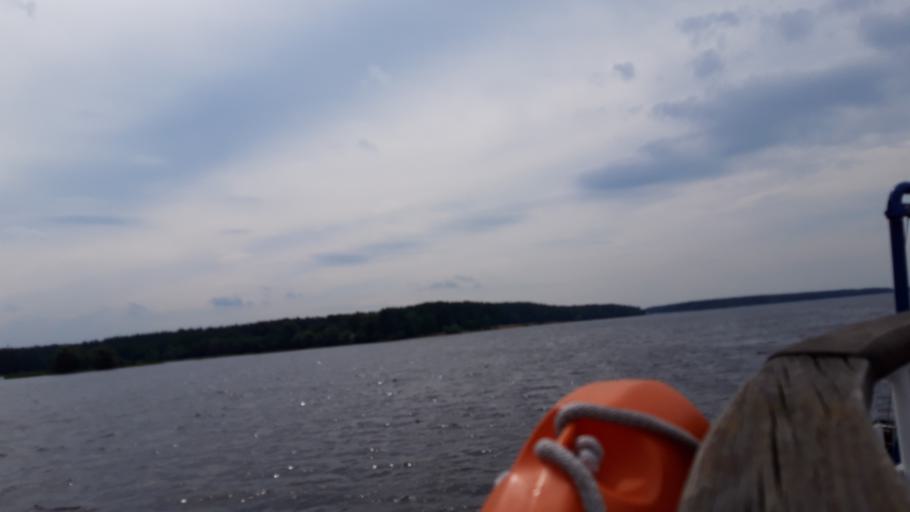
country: RU
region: Tverskaya
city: Konakovo
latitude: 56.7132
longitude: 36.7570
